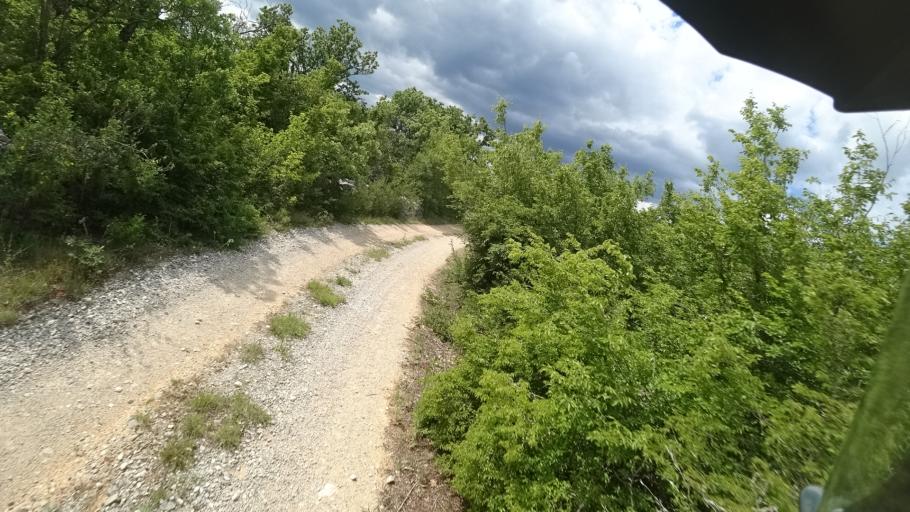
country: HR
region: Sibensko-Kniniska
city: Kistanje
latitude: 44.0910
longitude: 16.0400
